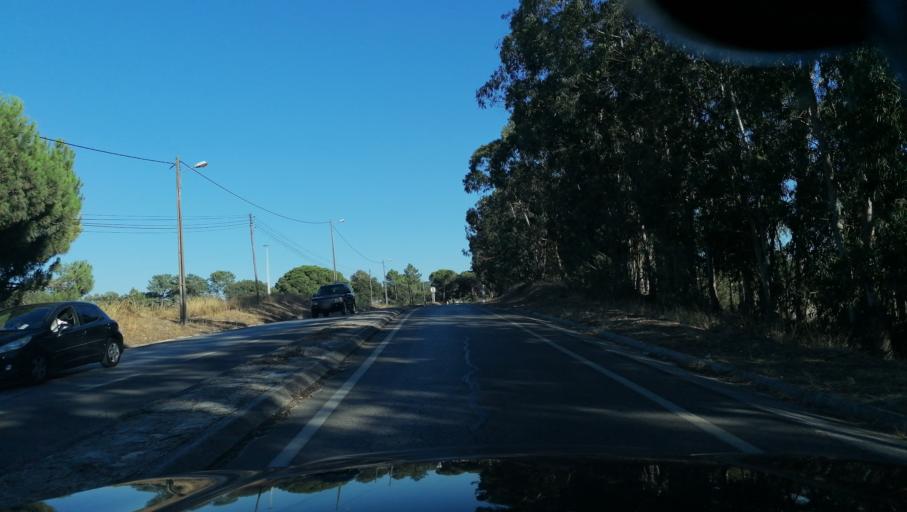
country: PT
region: Setubal
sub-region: Moita
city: Moita
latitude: 38.6315
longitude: -8.9680
